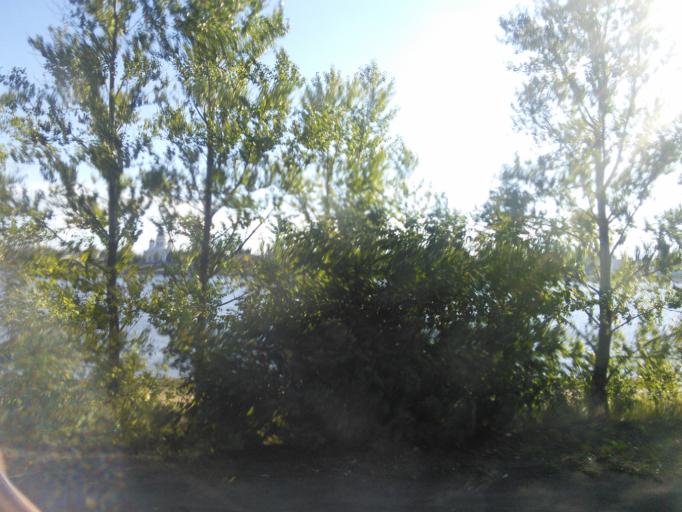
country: RU
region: Jaroslavl
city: Rybinsk
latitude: 58.0554
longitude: 38.8592
